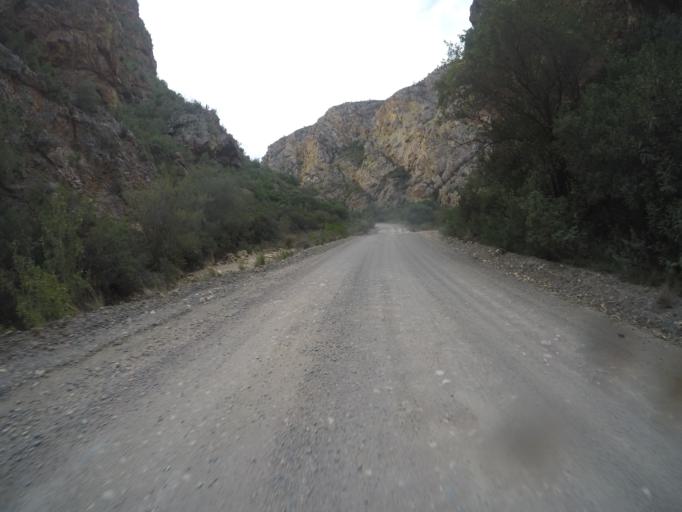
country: ZA
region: Eastern Cape
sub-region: Cacadu District Municipality
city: Willowmore
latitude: -33.5209
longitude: 23.6509
